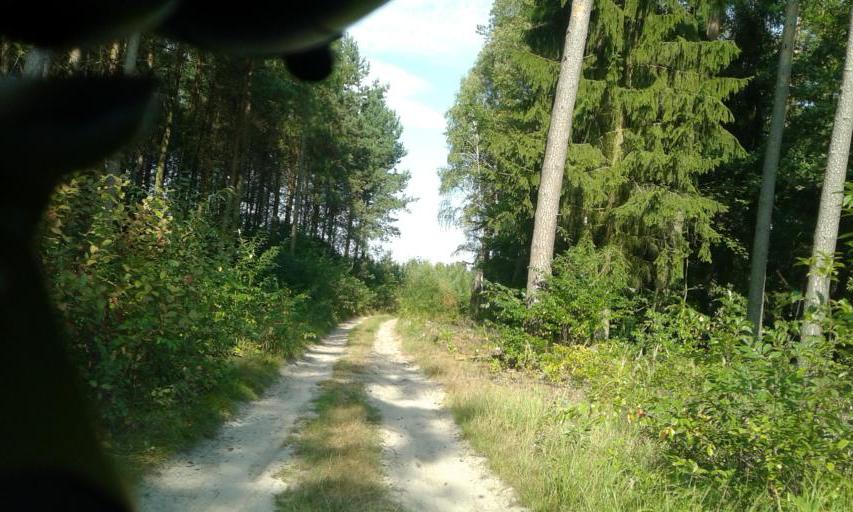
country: PL
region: West Pomeranian Voivodeship
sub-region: Powiat choszczenski
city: Krzecin
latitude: 53.0844
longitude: 15.4696
